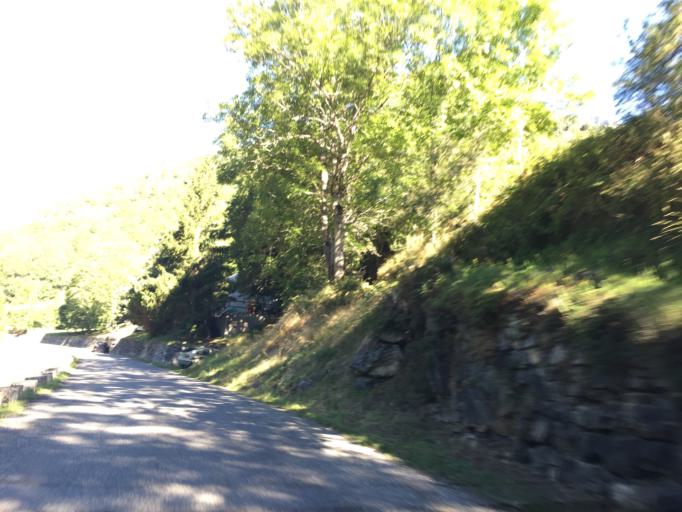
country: FR
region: Midi-Pyrenees
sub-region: Departement des Hautes-Pyrenees
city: Saint-Lary-Soulan
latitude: 42.8497
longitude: 0.2954
